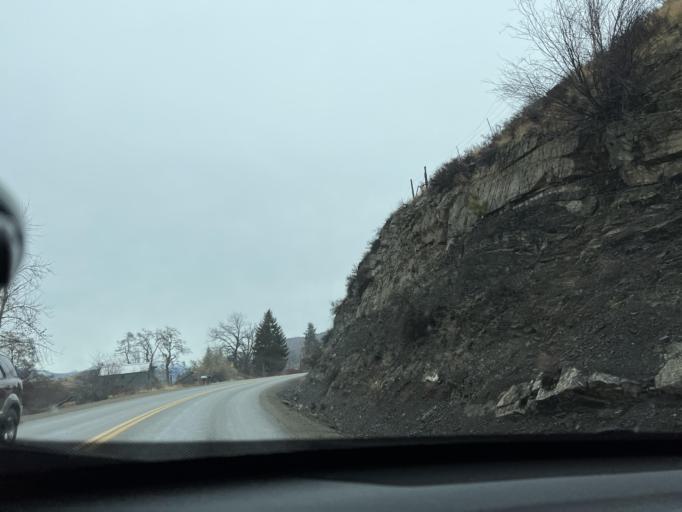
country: US
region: Washington
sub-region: Okanogan County
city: Brewster
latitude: 48.4908
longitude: -120.1795
